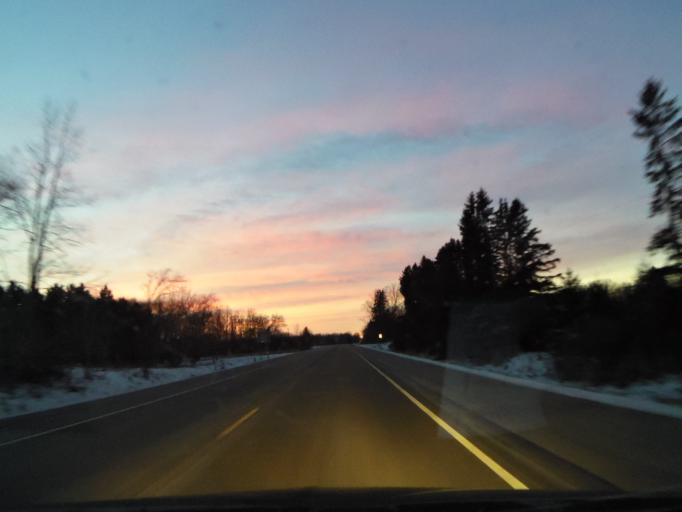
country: US
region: Minnesota
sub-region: Chisago County
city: Shafer
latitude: 45.3829
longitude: -92.7094
